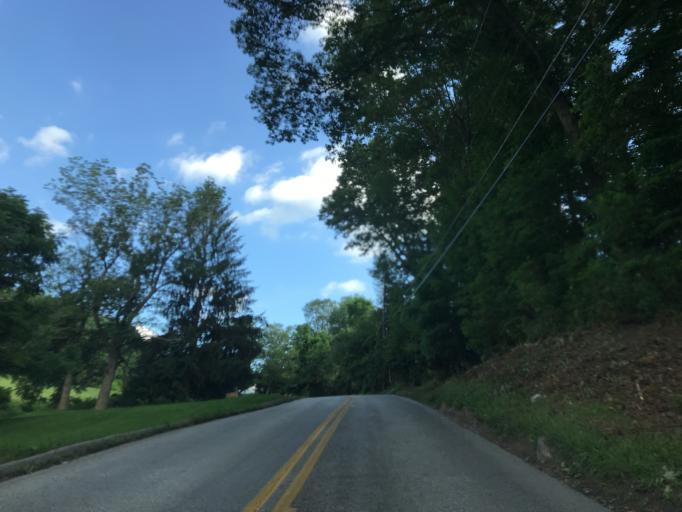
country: US
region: Maryland
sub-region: Carroll County
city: Hampstead
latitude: 39.6527
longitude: -76.8084
